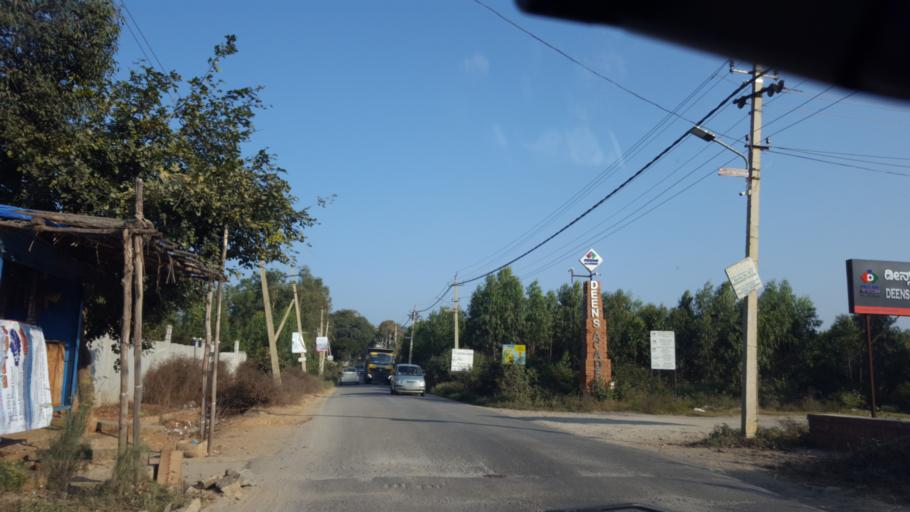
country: IN
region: Karnataka
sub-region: Bangalore Rural
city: Hoskote
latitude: 12.9171
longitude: 77.7619
